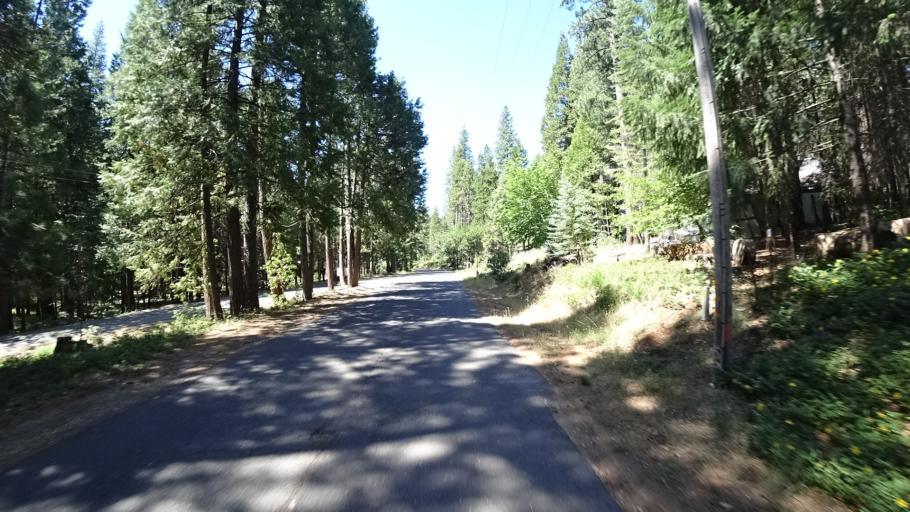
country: US
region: California
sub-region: Amador County
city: Pioneer
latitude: 38.4391
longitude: -120.4324
